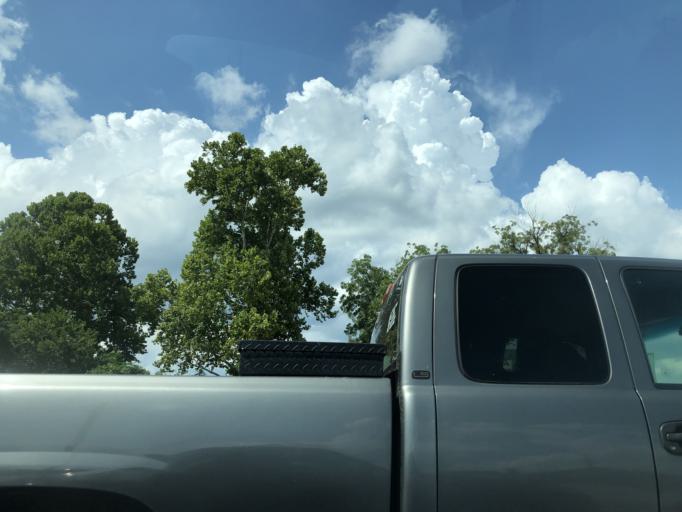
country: US
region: Georgia
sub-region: Telfair County
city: McRae
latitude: 32.0682
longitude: -82.9014
